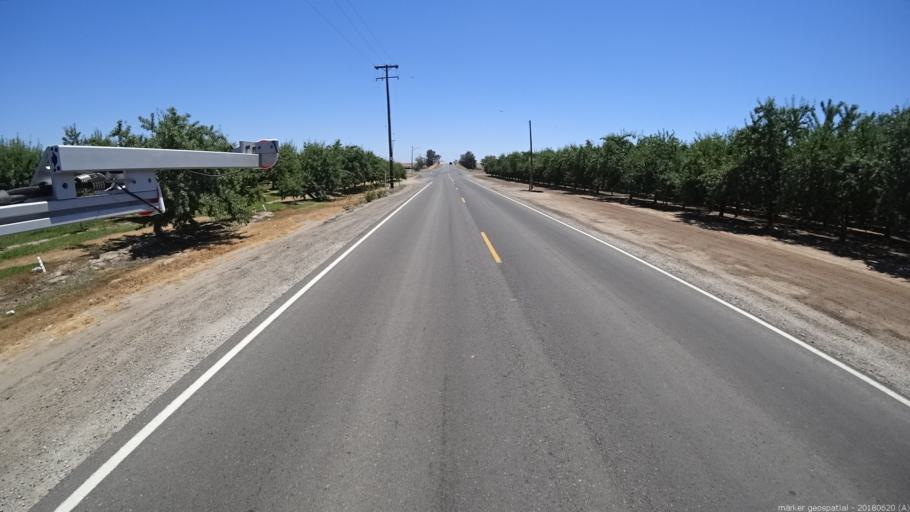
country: US
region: California
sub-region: Madera County
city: Parksdale
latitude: 36.8802
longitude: -119.9805
